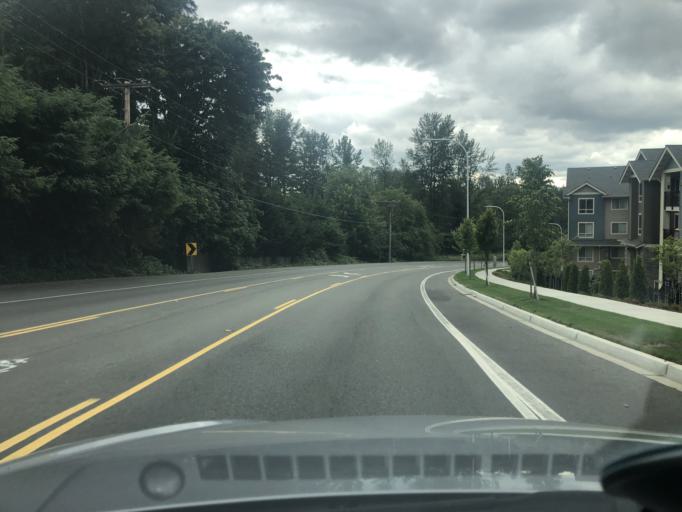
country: US
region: Washington
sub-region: King County
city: Lea Hill
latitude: 47.3233
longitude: -122.1664
